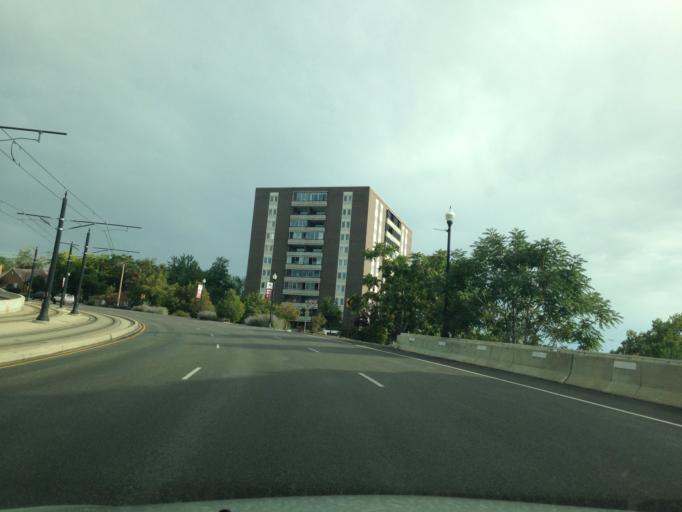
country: US
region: Utah
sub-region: Salt Lake County
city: Salt Lake City
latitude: 40.7593
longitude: -111.8626
